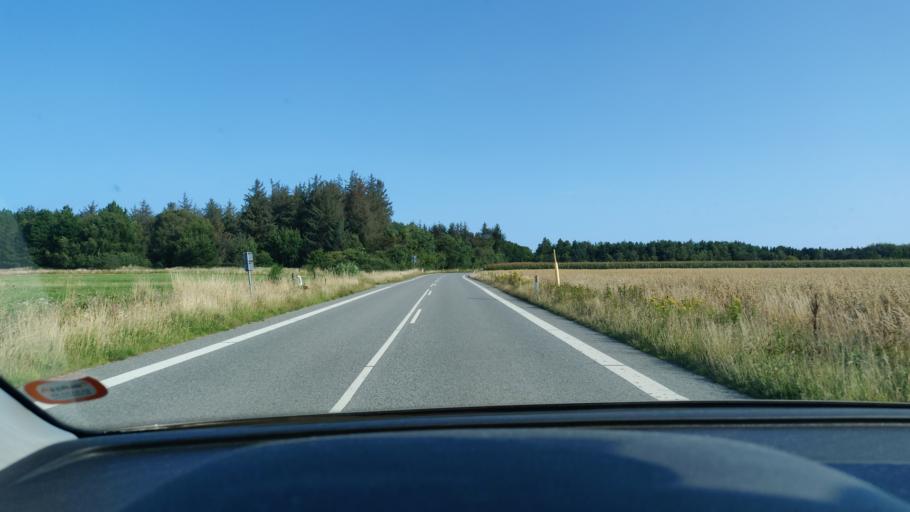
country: DK
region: North Denmark
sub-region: Jammerbugt Kommune
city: Pandrup
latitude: 57.2467
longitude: 9.6457
